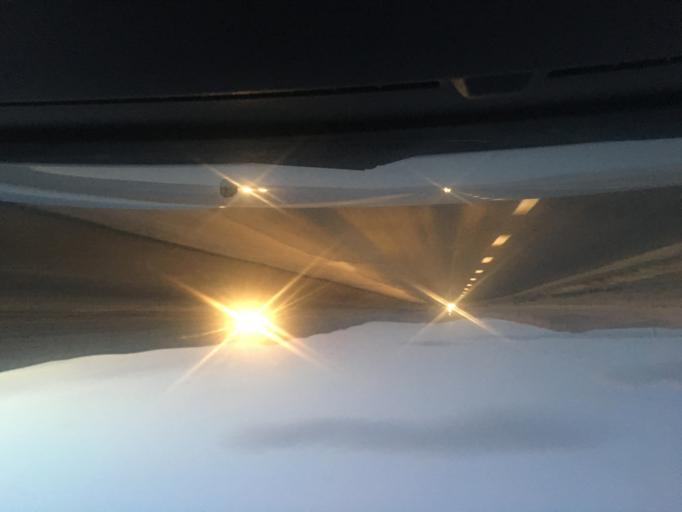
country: MN
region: Central Aimak
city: Altanbulag
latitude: 47.9927
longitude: 106.5563
